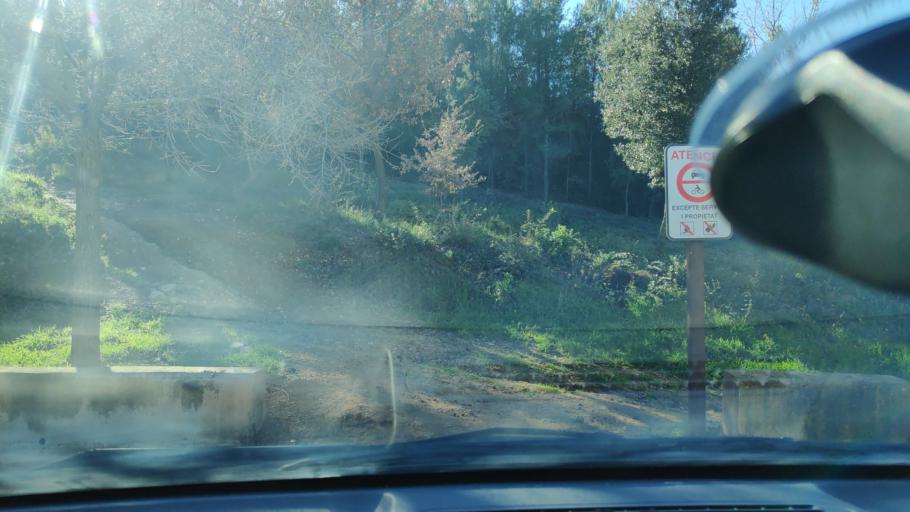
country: ES
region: Catalonia
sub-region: Provincia de Barcelona
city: Sant Quirze del Valles
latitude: 41.5255
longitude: 2.0671
